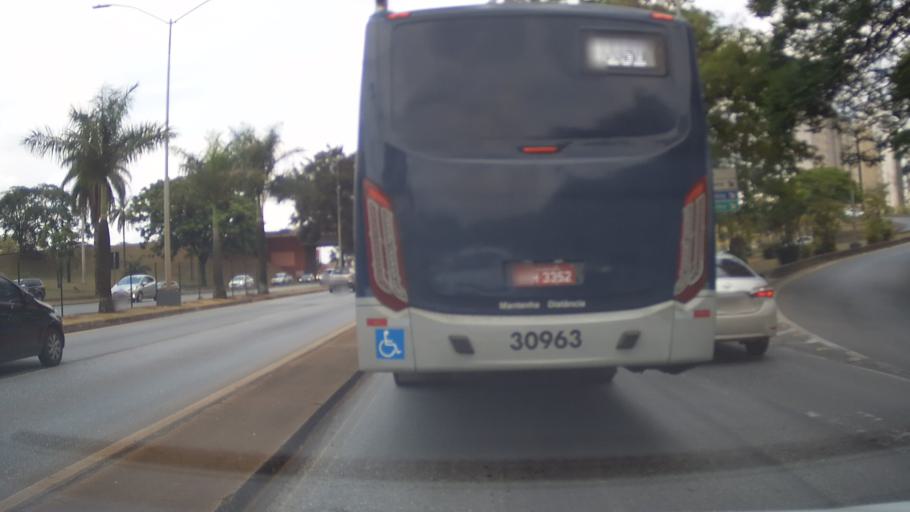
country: BR
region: Minas Gerais
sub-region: Belo Horizonte
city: Belo Horizonte
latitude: -19.9737
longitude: -43.9461
